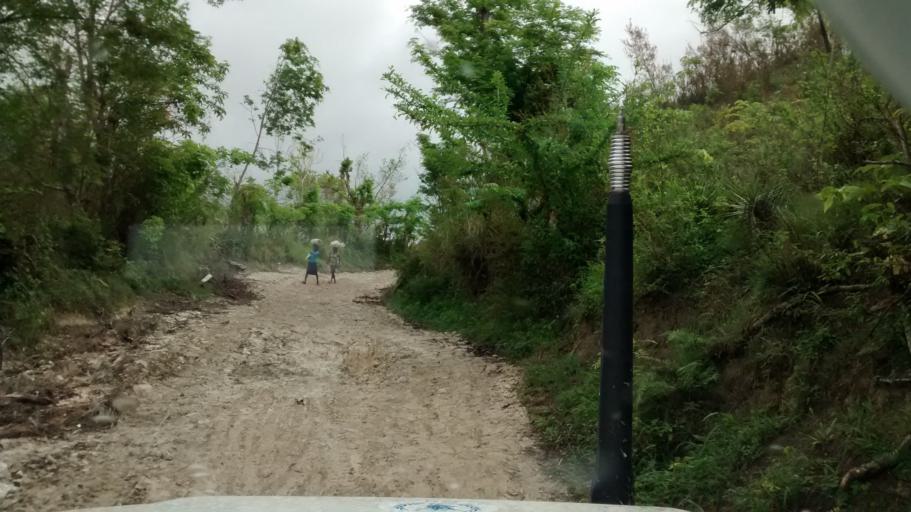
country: HT
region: Grandans
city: Jeremie
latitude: 18.5899
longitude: -74.1431
